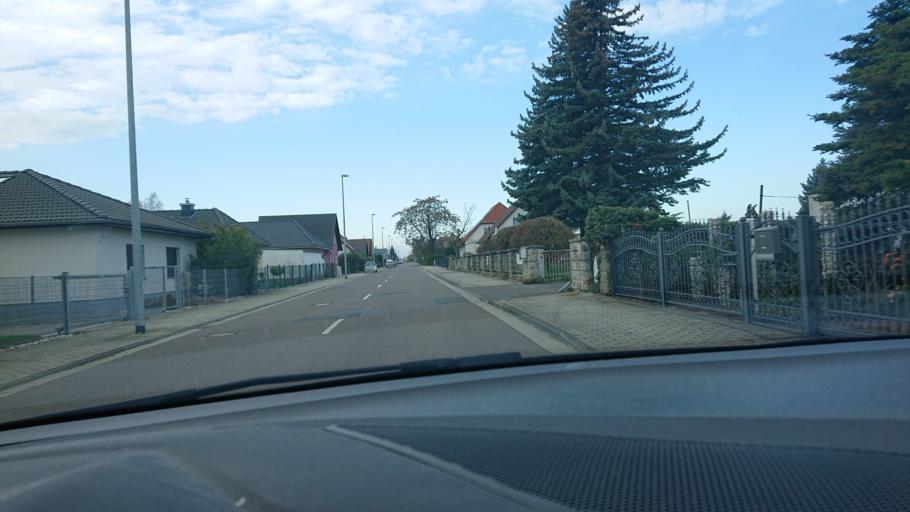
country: DE
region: Saxony
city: Delitzsch
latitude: 51.5202
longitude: 12.3190
